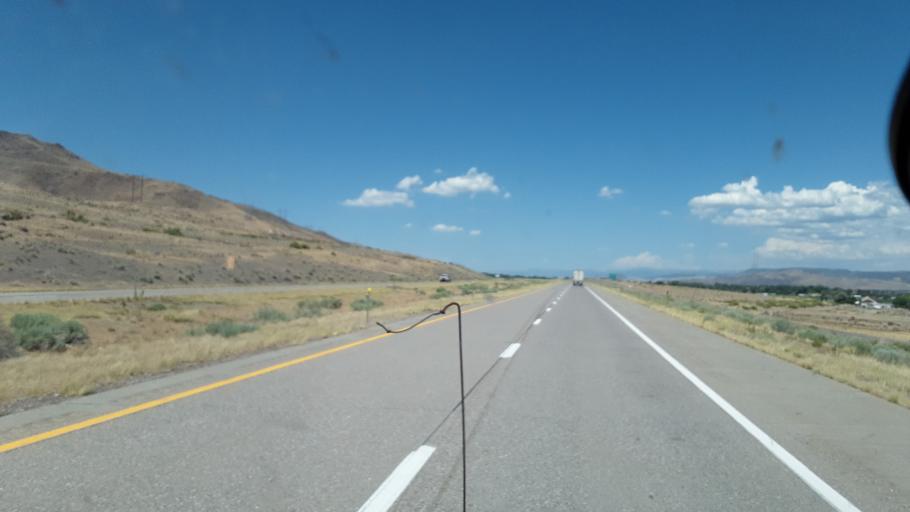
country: US
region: Utah
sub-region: Sevier County
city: Monroe
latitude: 38.6678
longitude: -112.1687
